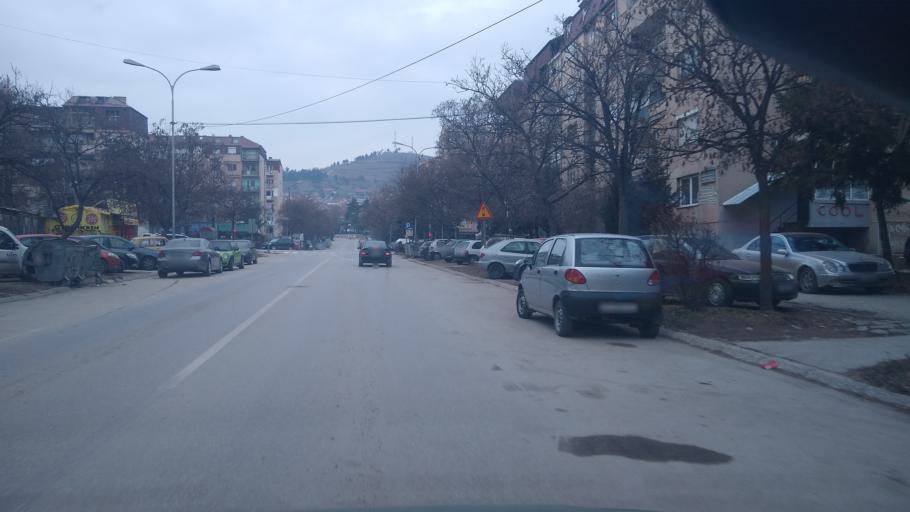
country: MK
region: Bitola
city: Bitola
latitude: 41.0345
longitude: 21.3407
